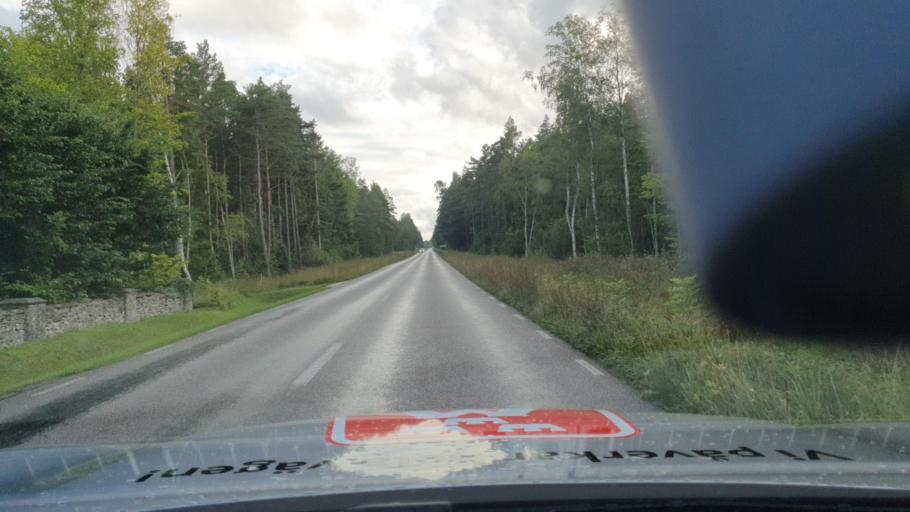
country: SE
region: Gotland
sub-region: Gotland
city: Slite
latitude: 57.6412
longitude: 18.7664
